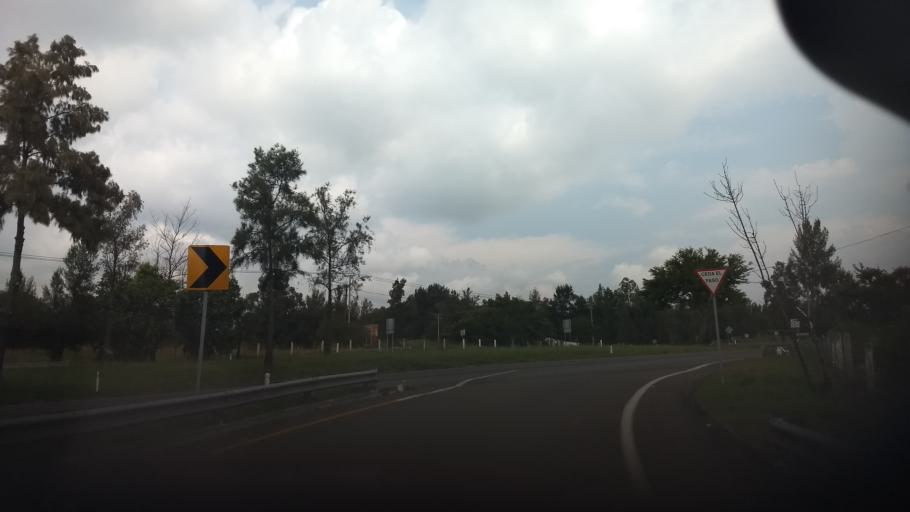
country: MX
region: Colima
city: Cofradia
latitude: 19.4012
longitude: -103.5371
